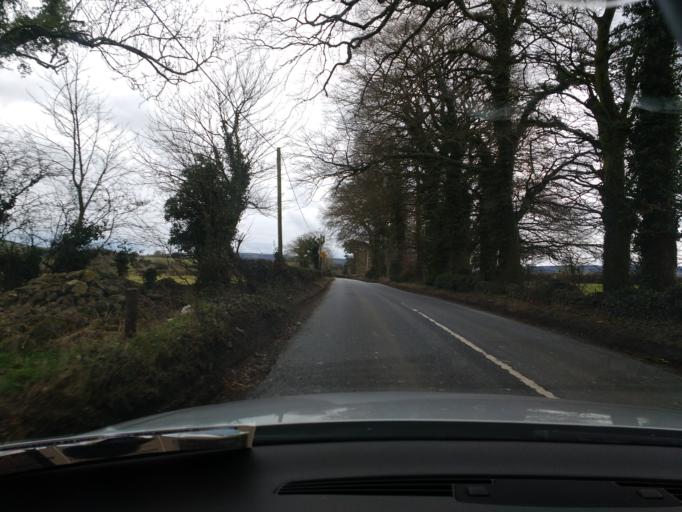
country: IE
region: Leinster
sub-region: Laois
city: Rathdowney
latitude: 52.7233
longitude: -7.5635
